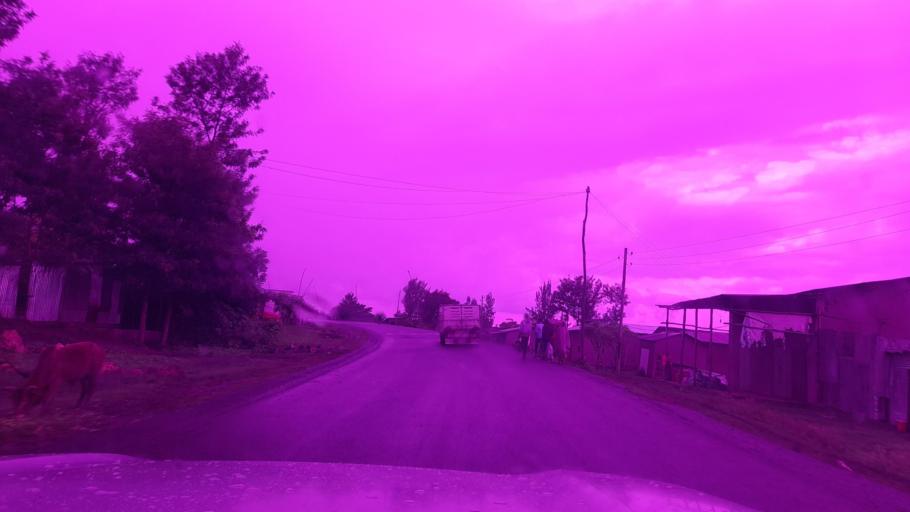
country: ET
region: Oromiya
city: Jima
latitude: 7.7146
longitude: 37.0983
